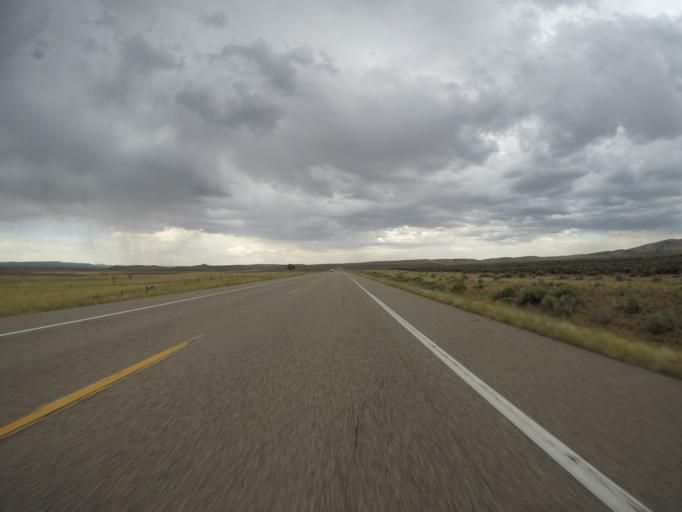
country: US
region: Colorado
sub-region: Rio Blanco County
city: Meeker
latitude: 40.4171
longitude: -108.3273
